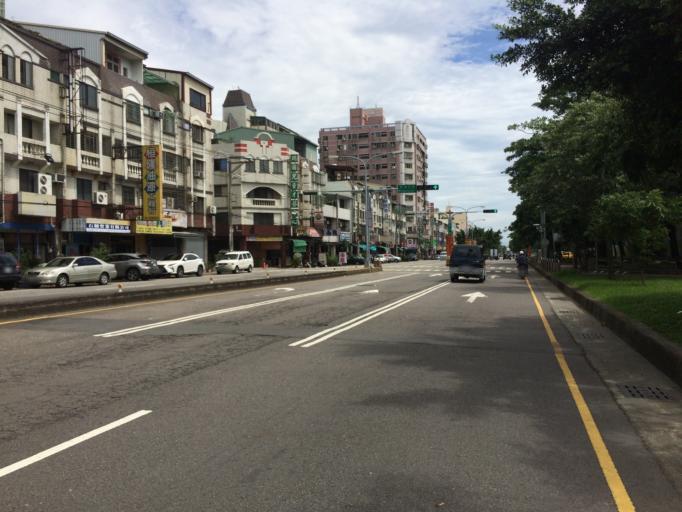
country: TW
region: Taiwan
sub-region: Taichung City
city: Taichung
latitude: 24.1538
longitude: 120.6990
